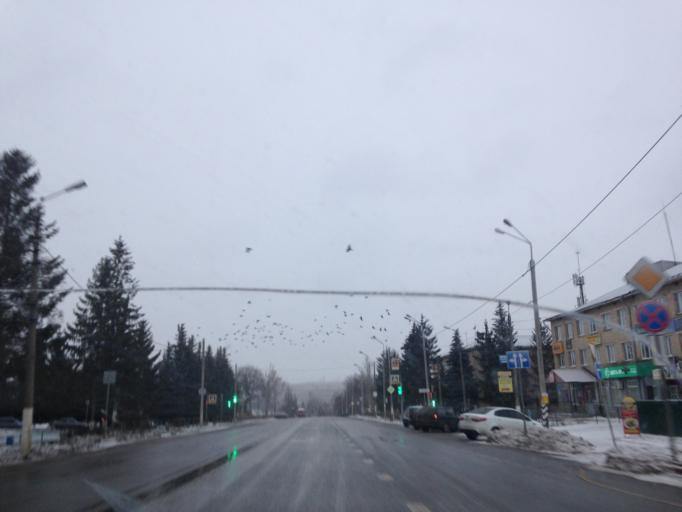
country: RU
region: Tula
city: Plavsk
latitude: 53.7056
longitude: 37.2913
